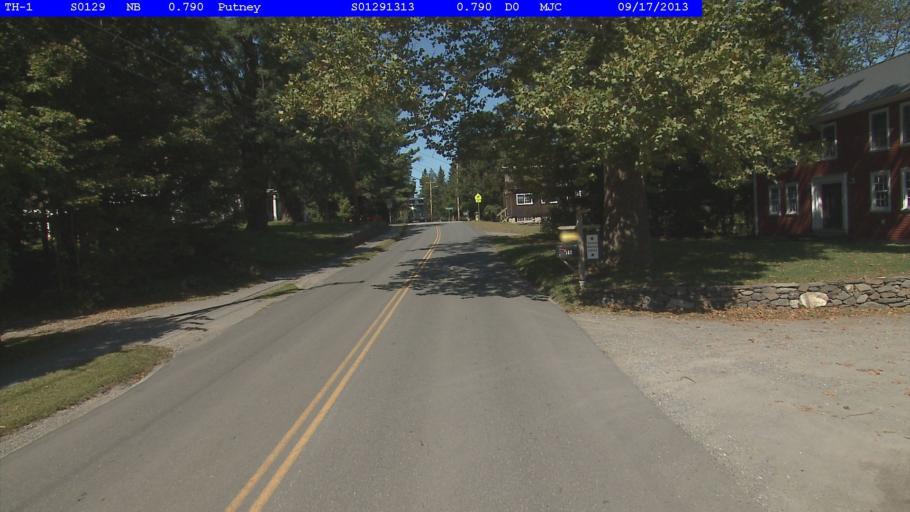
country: US
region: New Hampshire
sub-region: Cheshire County
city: Westmoreland
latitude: 42.9843
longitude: -72.5284
